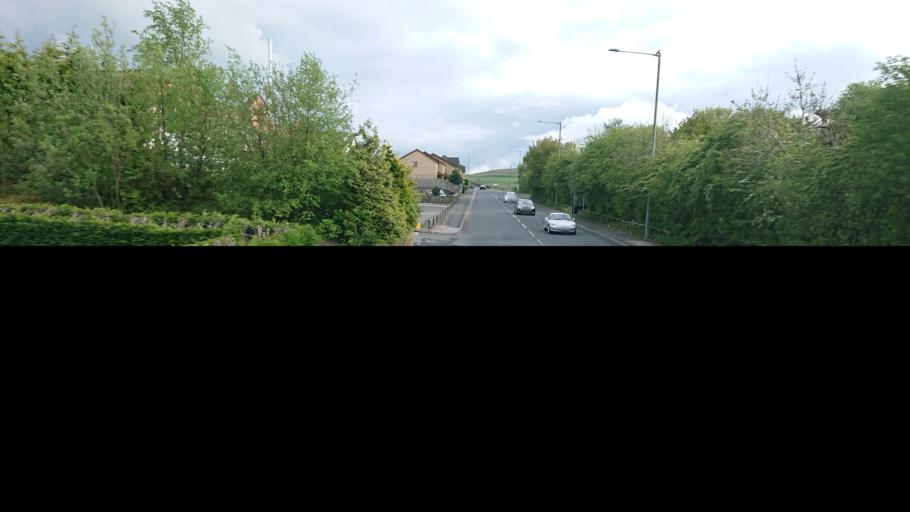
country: GB
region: England
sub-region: Lancashire
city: Burnley
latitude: 53.7728
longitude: -2.2574
